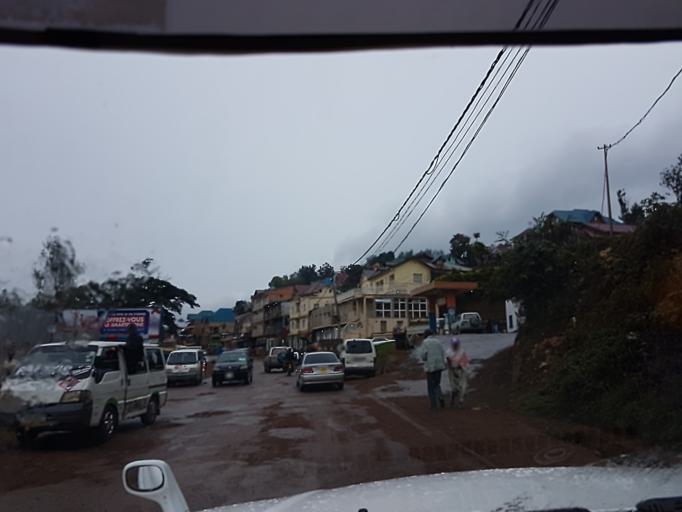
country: CD
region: South Kivu
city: Bukavu
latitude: -2.4962
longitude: 28.8503
